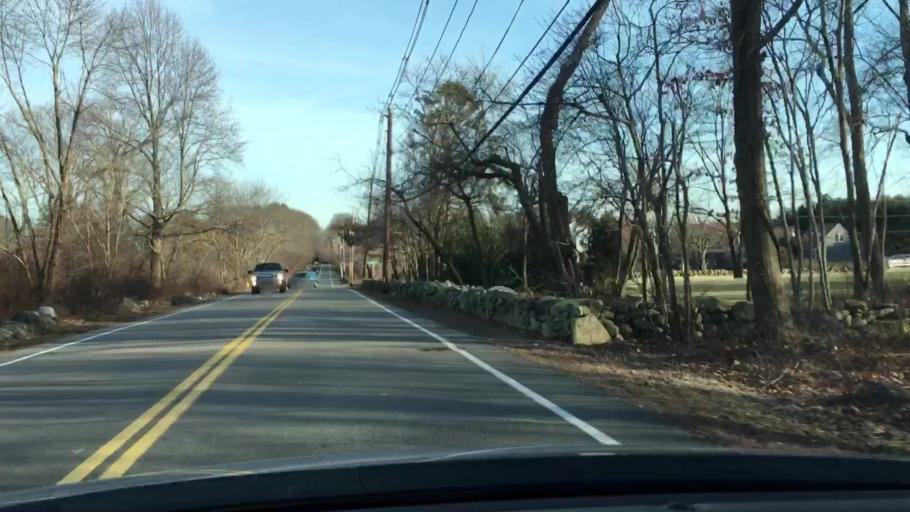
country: US
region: Massachusetts
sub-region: Norfolk County
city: Westwood
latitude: 42.2217
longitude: -71.2111
